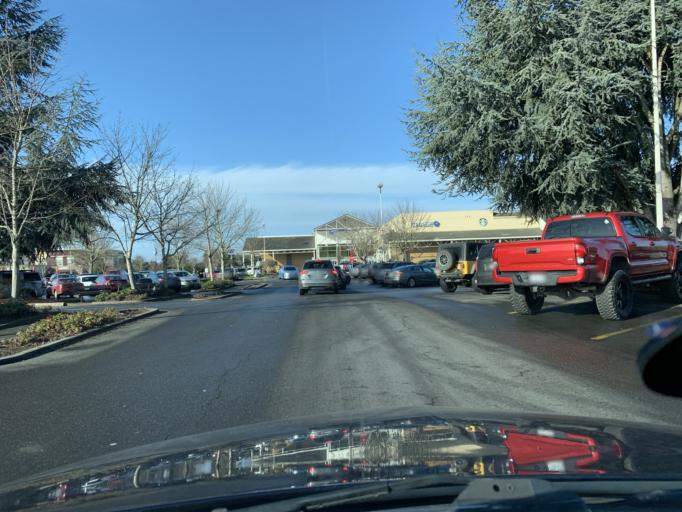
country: US
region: Washington
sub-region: Pierce County
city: North Puyallup
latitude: 47.2004
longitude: -122.2948
